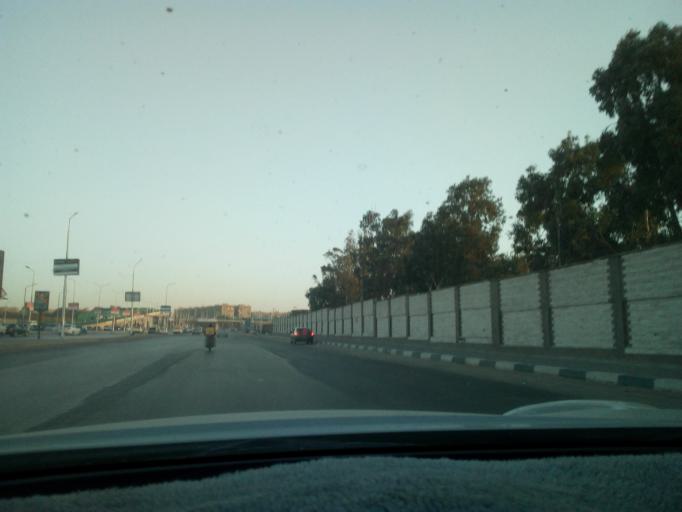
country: EG
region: Muhafazat al Qalyubiyah
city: Al Khankah
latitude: 30.1139
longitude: 31.3671
